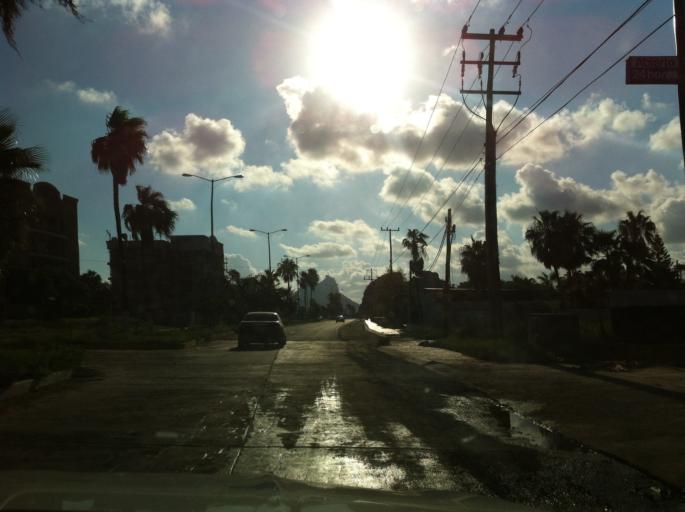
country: MX
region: Sonora
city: Heroica Guaymas
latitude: 27.9644
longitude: -111.0204
